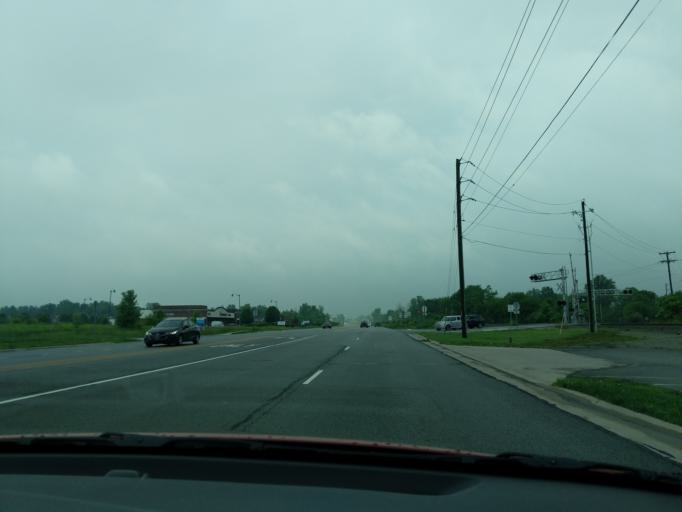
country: US
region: Indiana
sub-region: Hancock County
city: McCordsville
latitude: 39.8917
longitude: -85.9287
